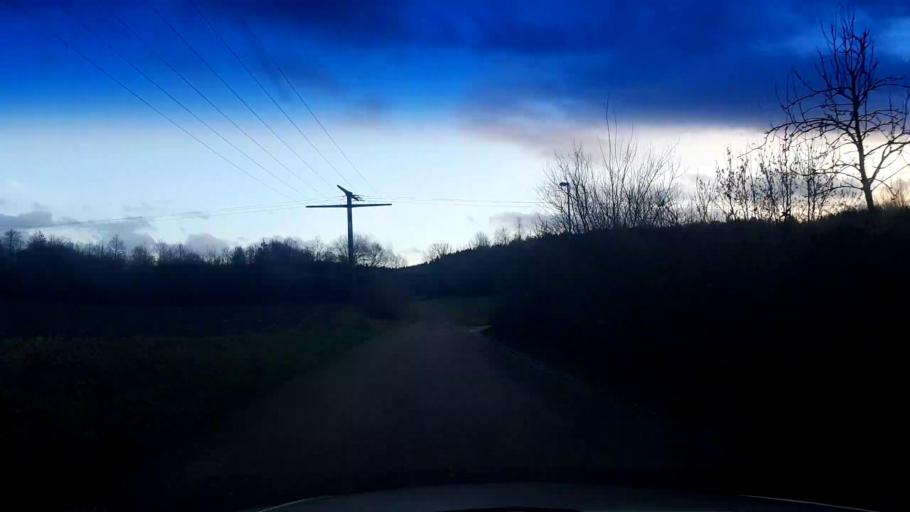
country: DE
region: Bavaria
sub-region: Upper Franconia
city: Buttenheim
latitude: 49.8070
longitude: 11.0590
